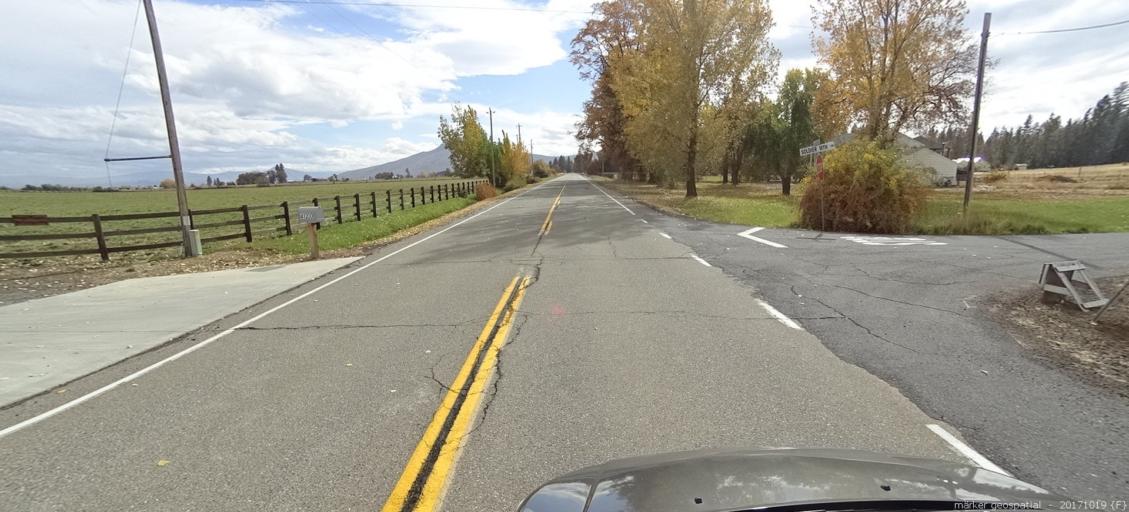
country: US
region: California
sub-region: Shasta County
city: Burney
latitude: 41.0896
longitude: -121.5143
